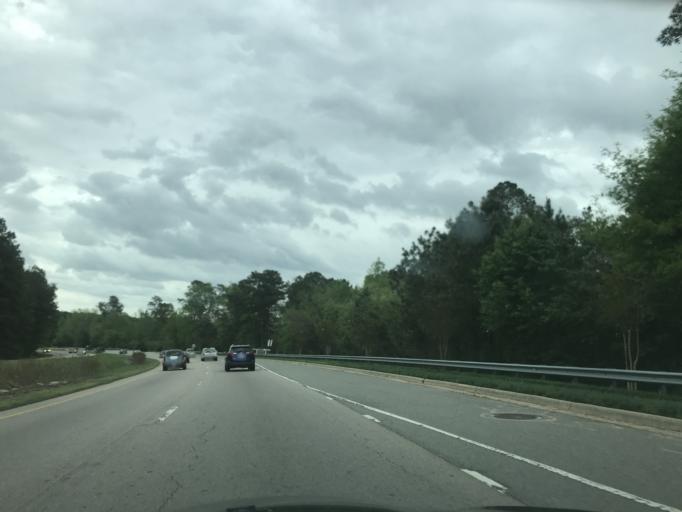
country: US
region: North Carolina
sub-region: Wake County
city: Knightdale
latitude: 35.7925
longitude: -78.5462
